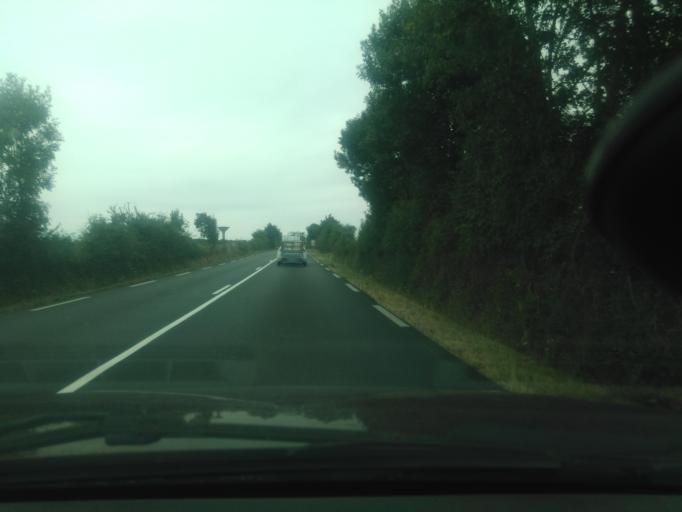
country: FR
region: Pays de la Loire
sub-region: Departement de la Vendee
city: Bazoges-en-Pareds
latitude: 46.6777
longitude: -0.9077
